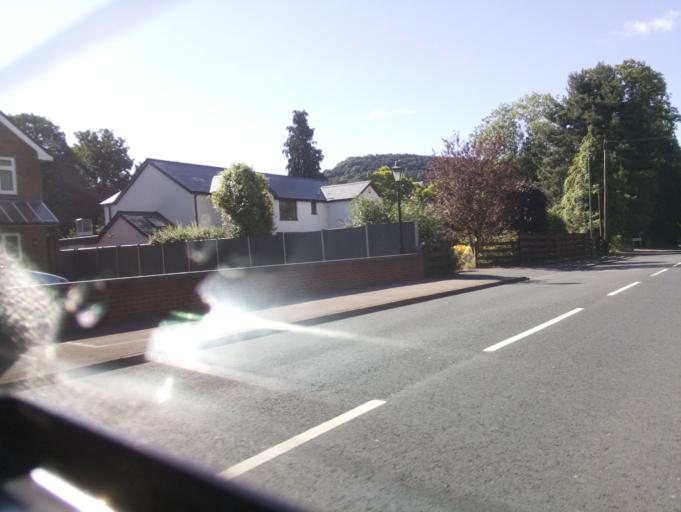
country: GB
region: England
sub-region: Herefordshire
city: Ross on Wye
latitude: 51.9077
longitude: -2.5861
